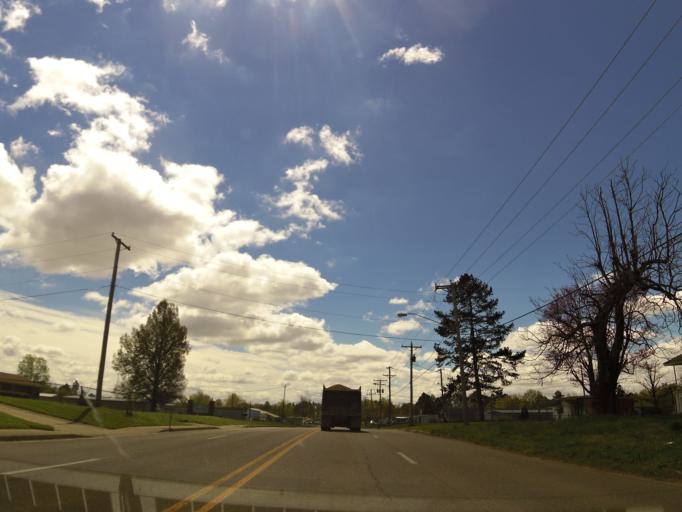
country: US
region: Arkansas
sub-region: Craighead County
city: Jonesboro
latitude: 35.8681
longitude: -90.7030
